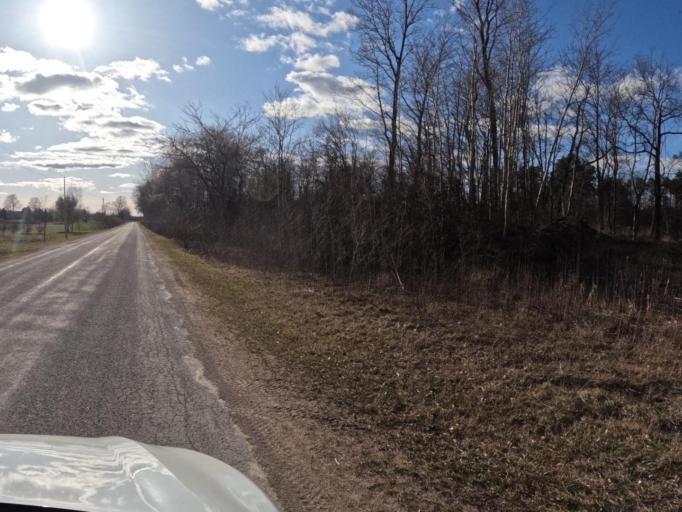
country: CA
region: Ontario
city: Norfolk County
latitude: 42.8154
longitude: -80.5602
